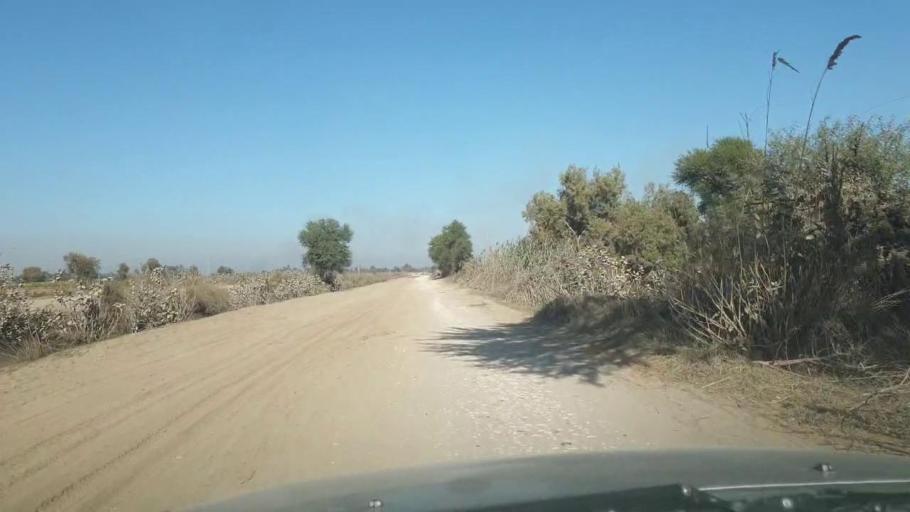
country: PK
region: Sindh
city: Ghotki
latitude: 28.0779
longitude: 69.3461
